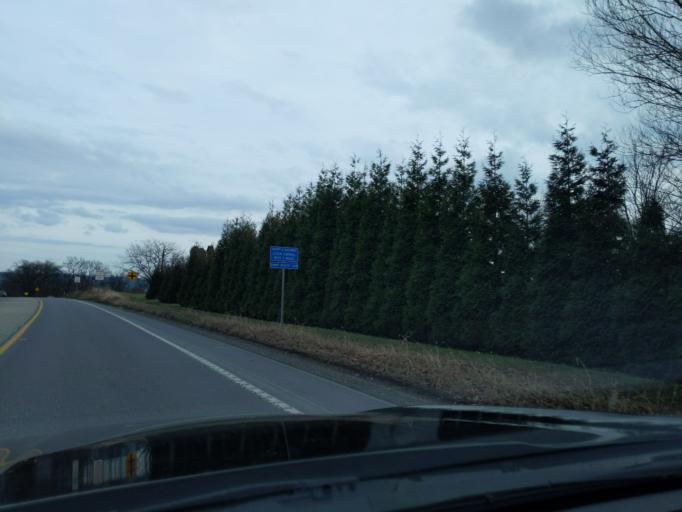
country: US
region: Pennsylvania
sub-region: Blair County
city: Lakemont
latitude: 40.4615
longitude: -78.3747
